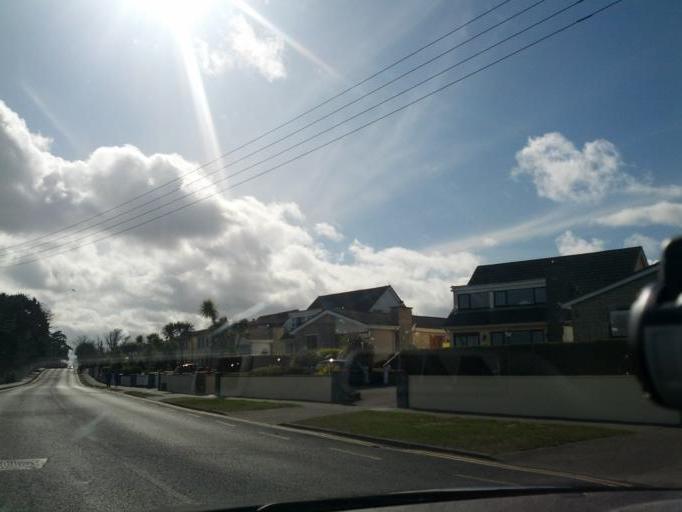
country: IE
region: Leinster
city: Portmarnock
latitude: 53.4321
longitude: -6.1249
